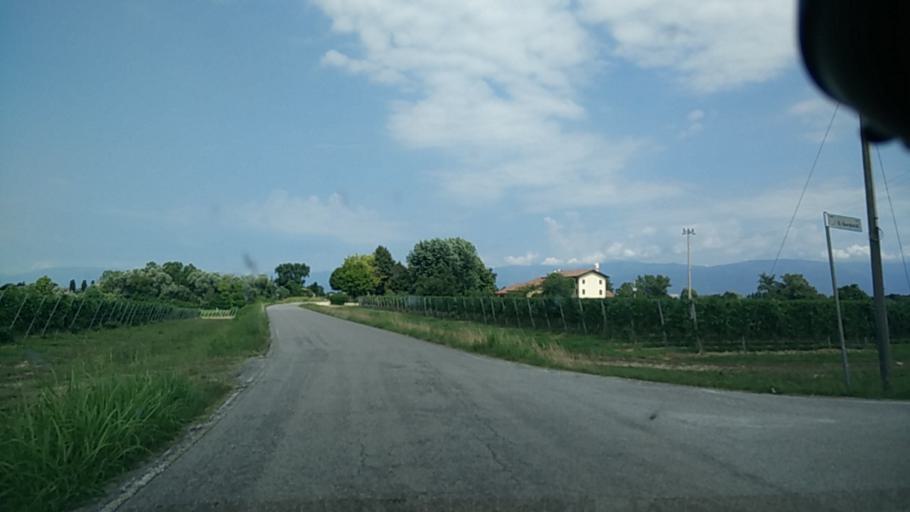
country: IT
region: Veneto
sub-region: Provincia di Treviso
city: Portobuffole
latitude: 45.8508
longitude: 12.5550
